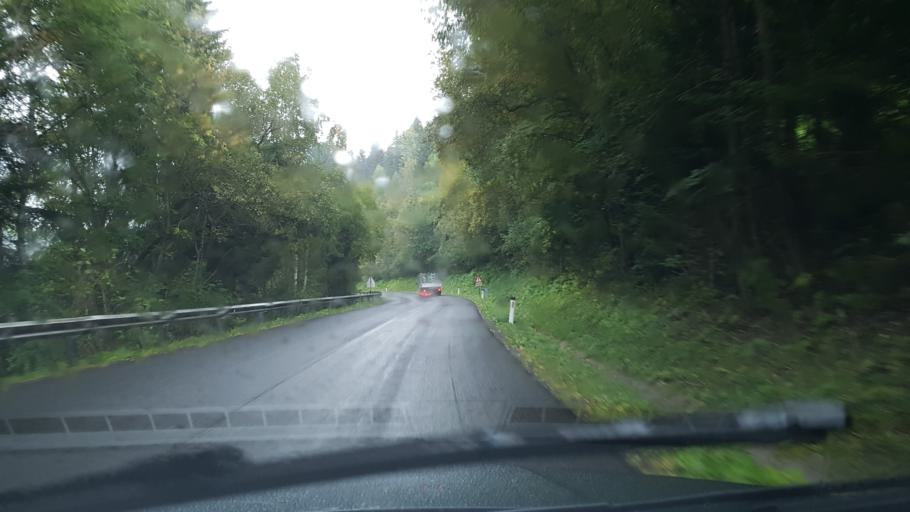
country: AT
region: Styria
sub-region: Politischer Bezirk Voitsberg
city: Salla
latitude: 47.1082
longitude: 14.9463
